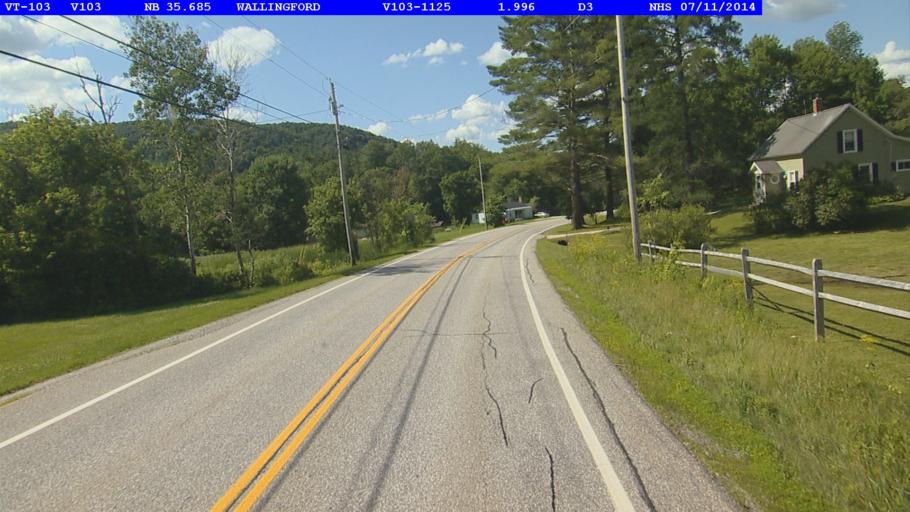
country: US
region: Vermont
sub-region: Rutland County
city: Rutland
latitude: 43.4782
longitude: -72.8776
